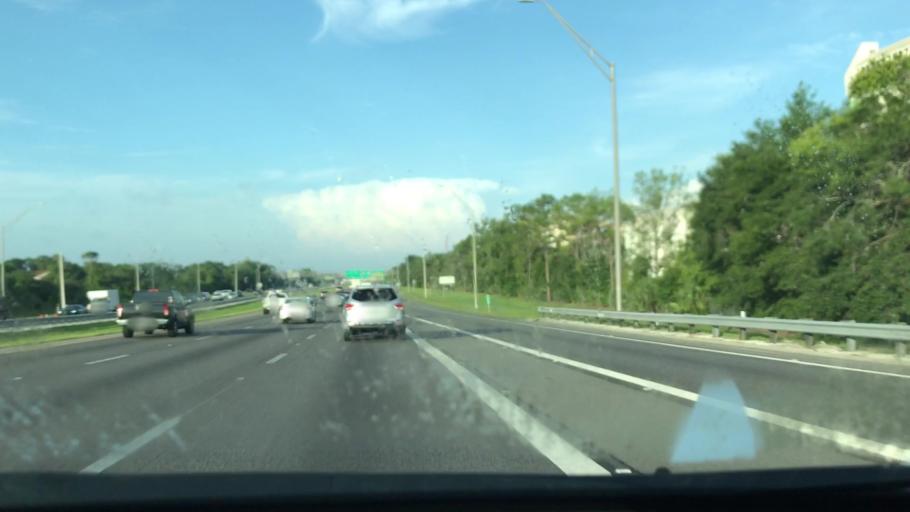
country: US
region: Florida
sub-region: Osceola County
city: Celebration
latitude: 28.3760
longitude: -81.5074
